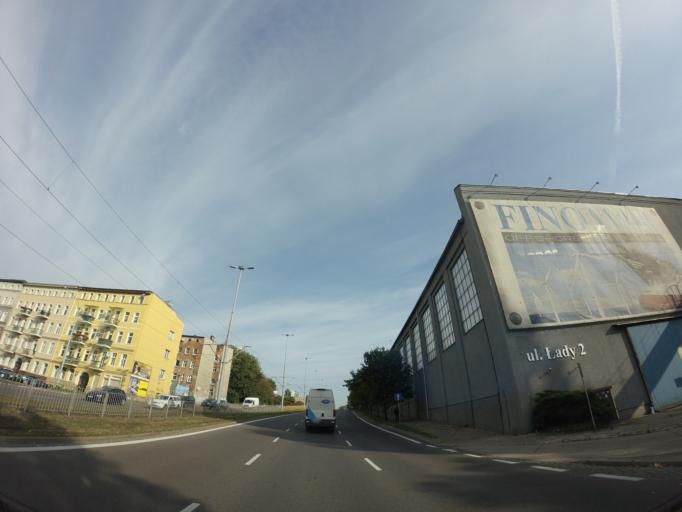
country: PL
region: West Pomeranian Voivodeship
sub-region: Szczecin
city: Szczecin
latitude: 53.4348
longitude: 14.5732
